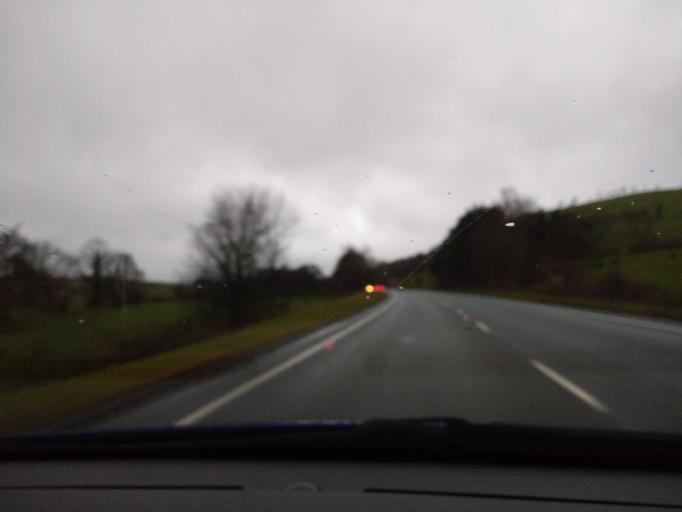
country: GB
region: England
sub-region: Cumbria
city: Cockermouth
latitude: 54.6595
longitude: -3.3161
